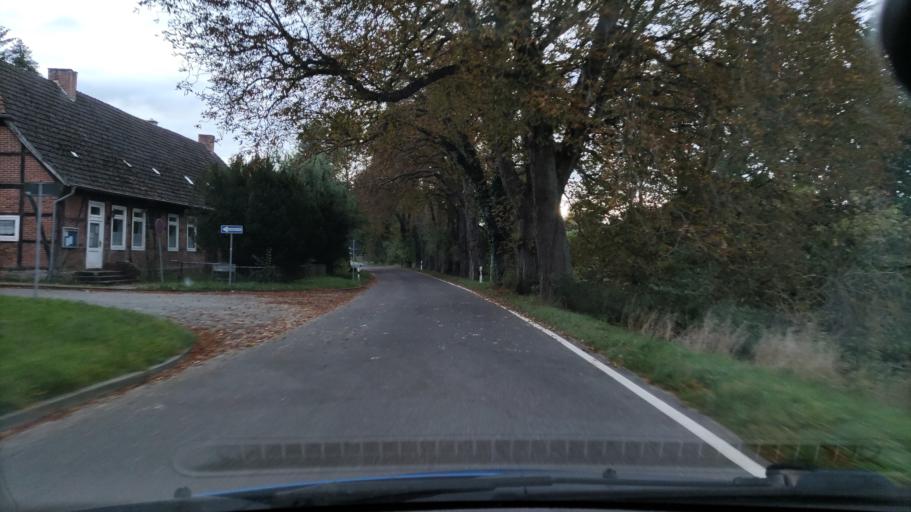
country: DE
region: Mecklenburg-Vorpommern
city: Zarrentin
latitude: 53.4617
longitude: 10.9641
